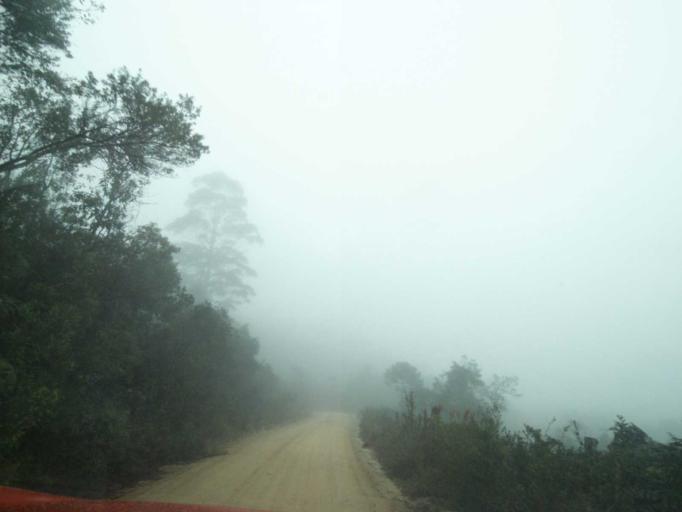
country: BR
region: Santa Catarina
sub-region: Anitapolis
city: Anitapolis
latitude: -27.9110
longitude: -49.1698
